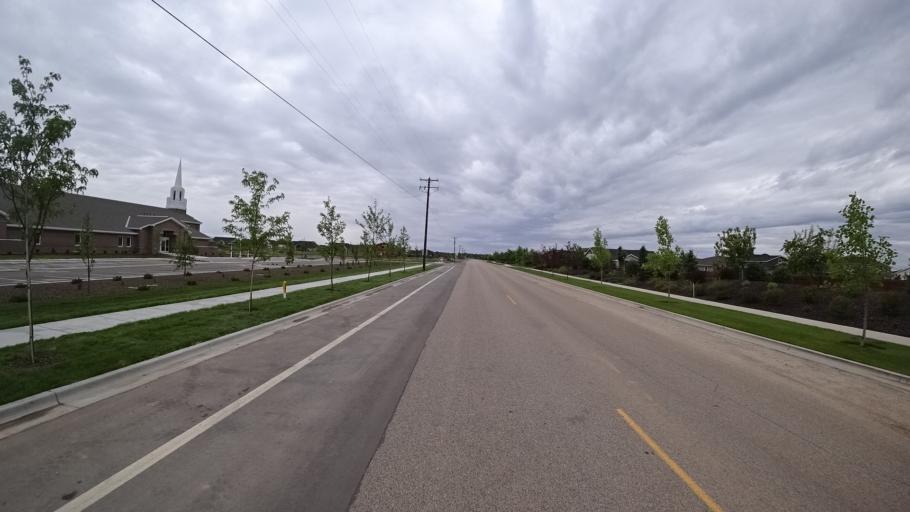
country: US
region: Idaho
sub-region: Ada County
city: Eagle
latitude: 43.7128
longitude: -116.4235
